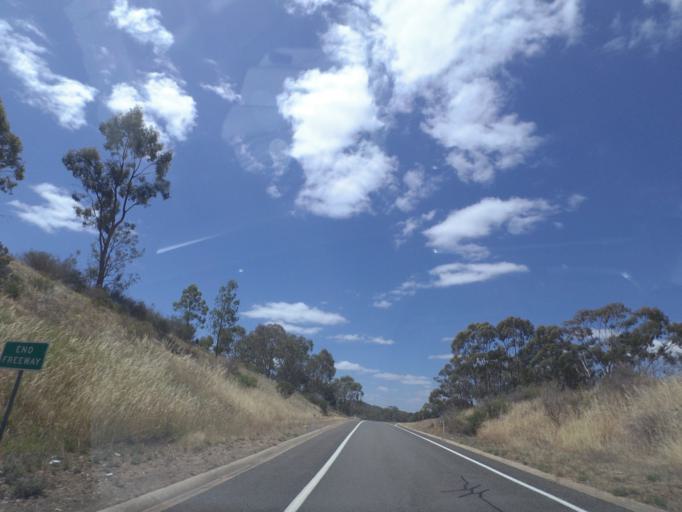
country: AU
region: Victoria
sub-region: Wangaratta
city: Wangaratta
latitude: -36.4673
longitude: 146.2097
